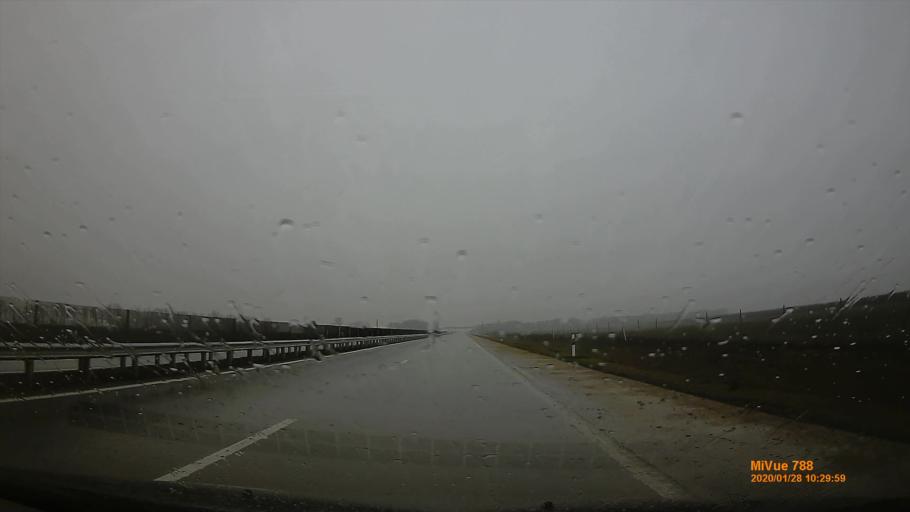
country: HU
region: Pest
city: Gomba
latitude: 47.3284
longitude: 19.5251
